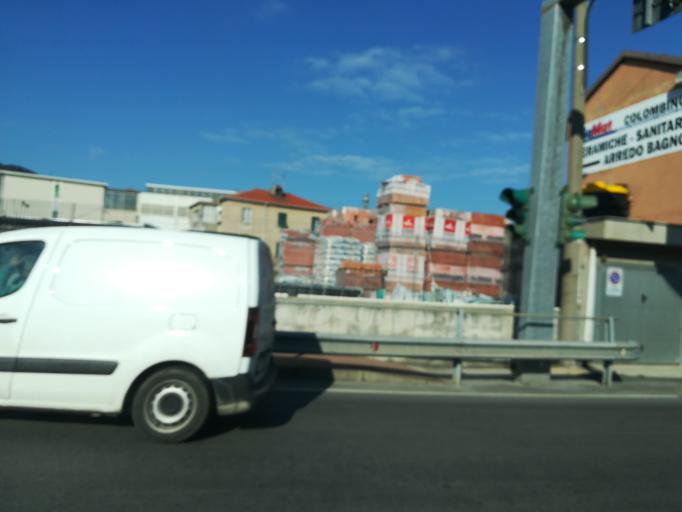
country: IT
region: Liguria
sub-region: Provincia di Savona
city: Vado Centro
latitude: 44.2656
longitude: 8.4266
